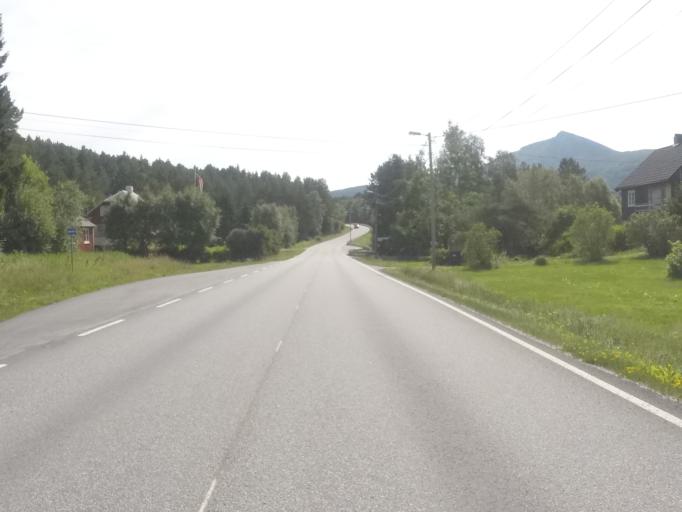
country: NO
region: More og Romsdal
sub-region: Averoy
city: Bruhagen
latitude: 63.0179
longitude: 7.5884
